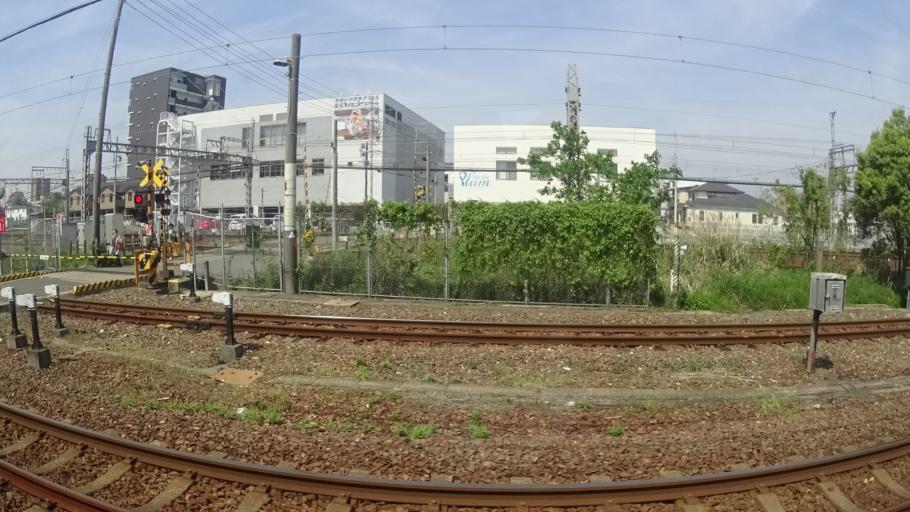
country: JP
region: Aichi
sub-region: Tsushima-shi
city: Tsushima
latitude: 35.0686
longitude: 136.6841
